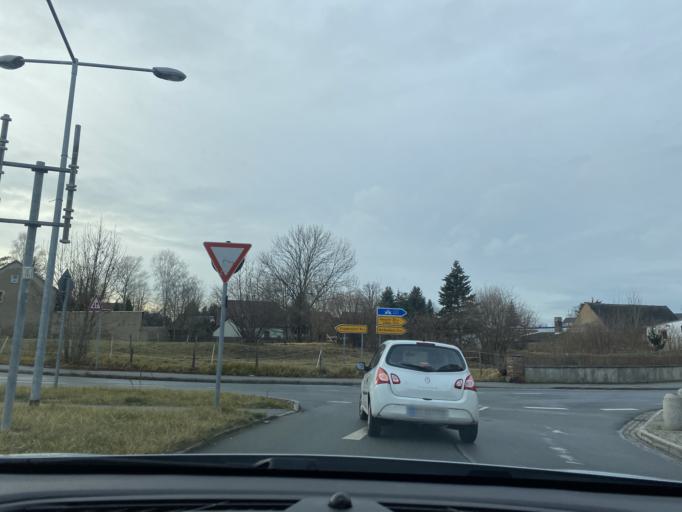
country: DE
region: Saxony
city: Reichenbach
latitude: 51.1408
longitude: 14.7985
